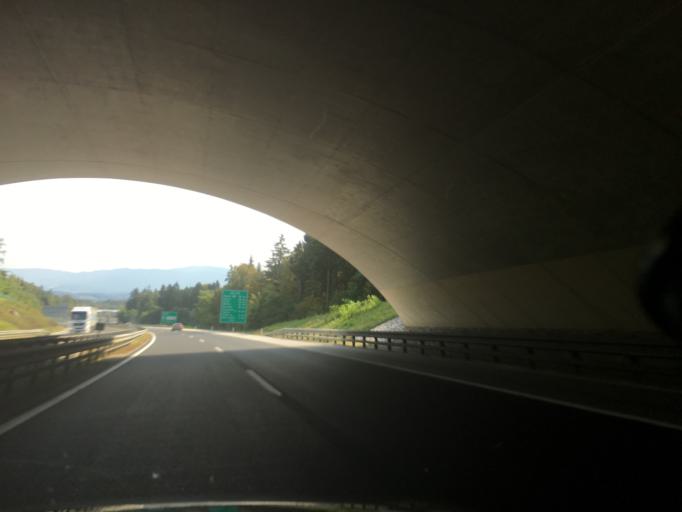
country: SI
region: Novo Mesto
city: Novo Mesto
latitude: 45.8380
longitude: 15.1618
